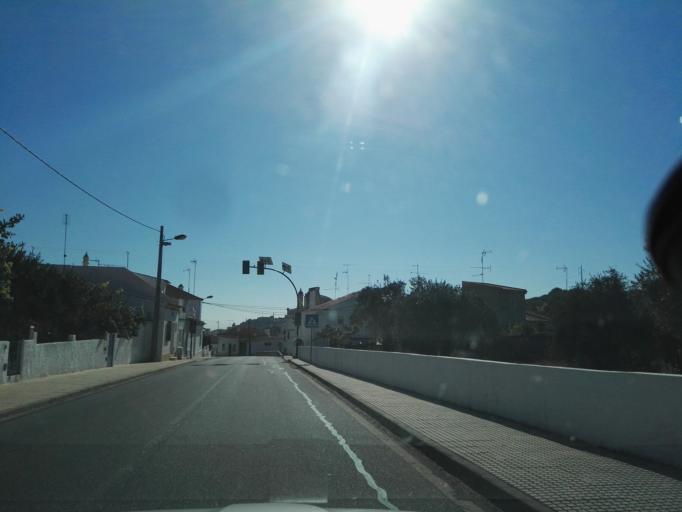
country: PT
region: Portalegre
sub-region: Elvas
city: Elvas
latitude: 38.8971
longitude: -7.1762
